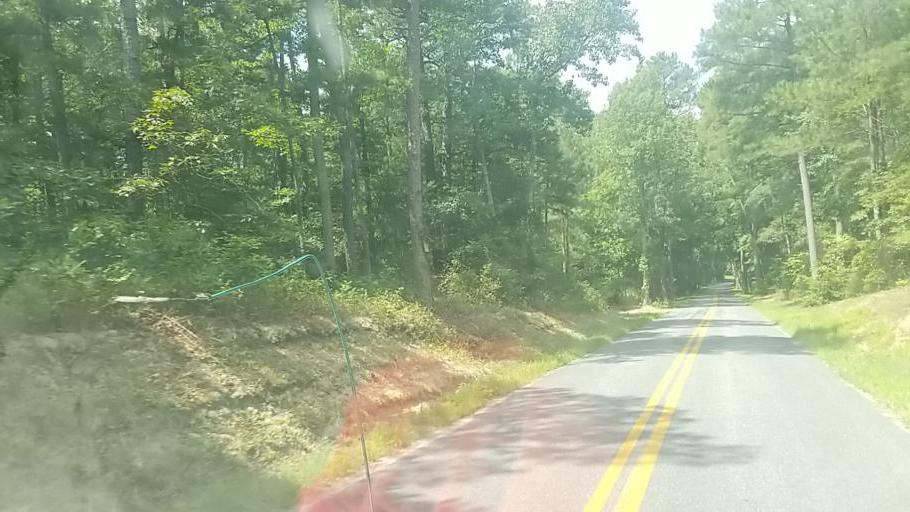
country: US
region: Maryland
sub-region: Worcester County
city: Snow Hill
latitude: 38.2625
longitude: -75.4597
